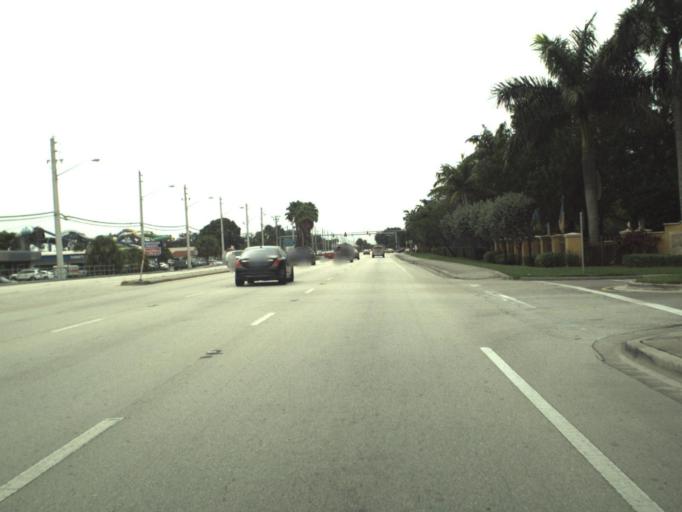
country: US
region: Florida
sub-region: Palm Beach County
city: Mangonia Park
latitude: 26.7763
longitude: -80.1077
